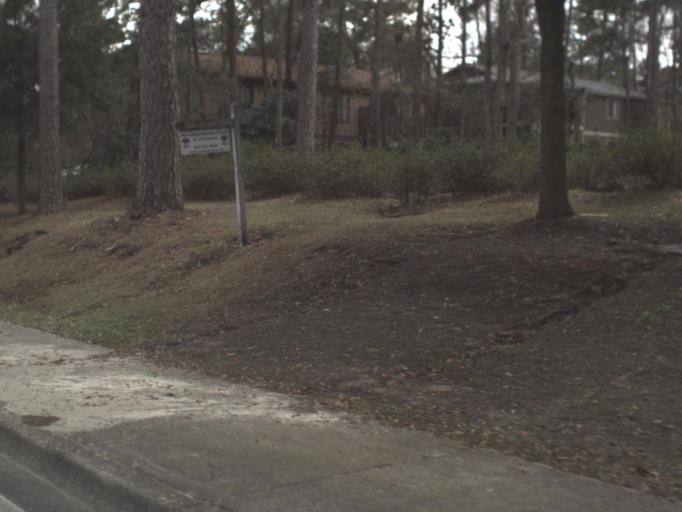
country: US
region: Florida
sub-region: Leon County
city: Tallahassee
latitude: 30.4721
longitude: -84.2773
